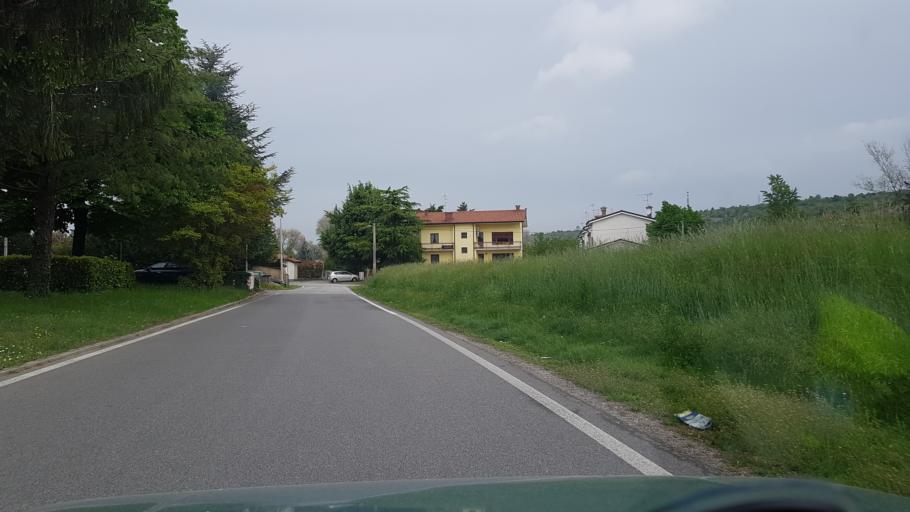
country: IT
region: Friuli Venezia Giulia
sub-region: Provincia di Gorizia
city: Ronchi dei Legionari
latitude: 45.8323
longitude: 13.5133
